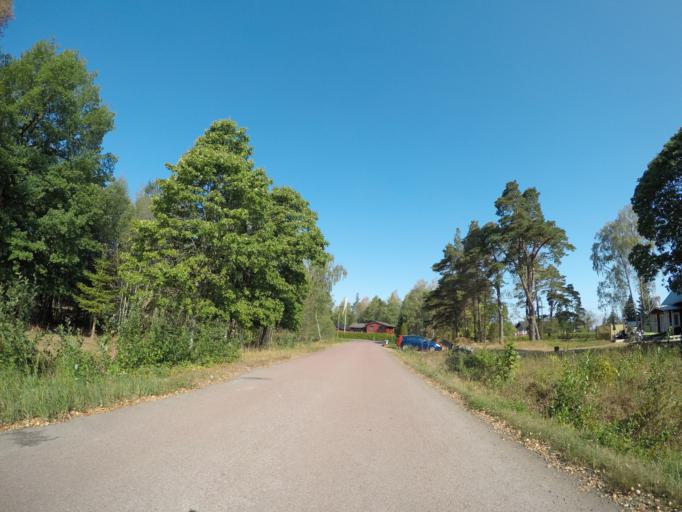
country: AX
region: Alands landsbygd
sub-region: Finstroem
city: Finstroem
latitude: 60.2722
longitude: 19.9395
